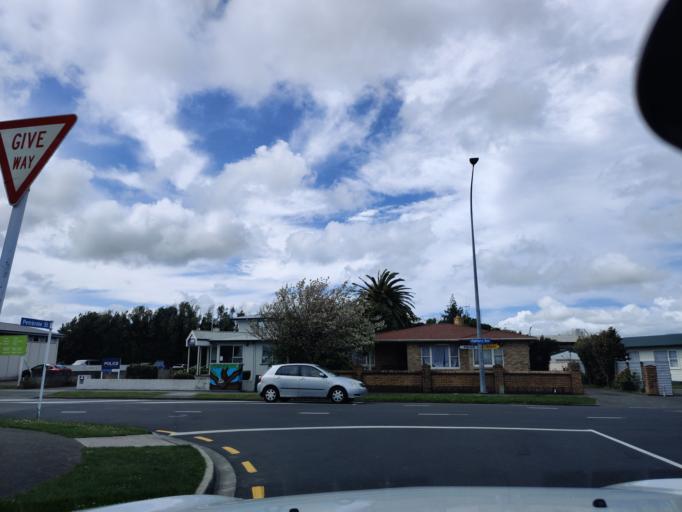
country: NZ
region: Manawatu-Wanganui
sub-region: Palmerston North City
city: Palmerston North
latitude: -40.3594
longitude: 175.5862
